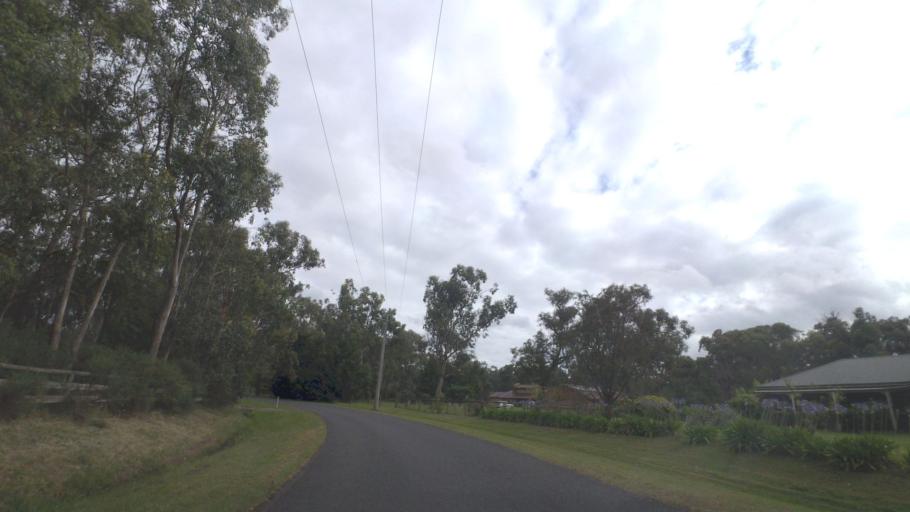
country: AU
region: Victoria
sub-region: Maroondah
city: Kilsyth South
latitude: -37.8243
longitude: 145.3104
